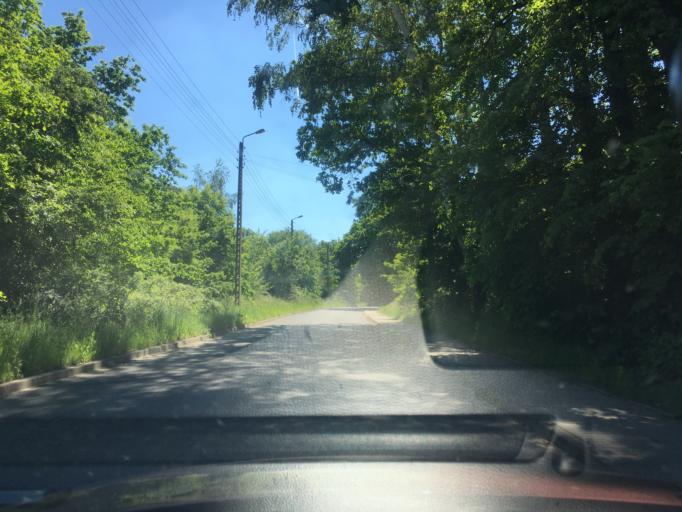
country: PL
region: Silesian Voivodeship
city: Zawidow
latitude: 51.0230
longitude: 15.0557
